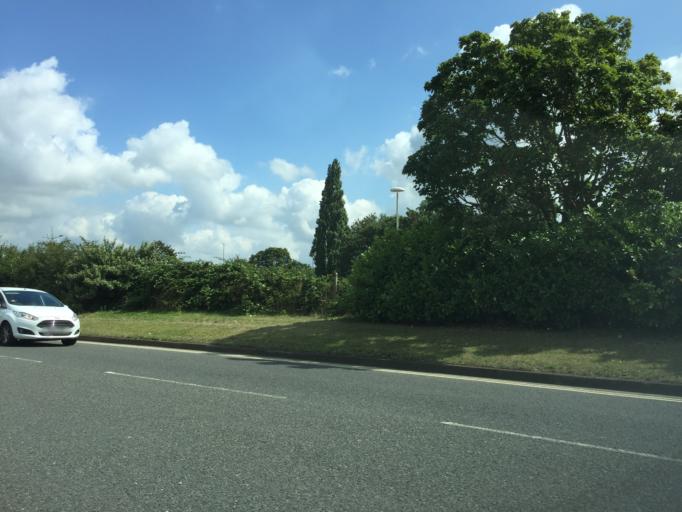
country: GB
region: England
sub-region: Gloucestershire
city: Gloucester
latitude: 51.8689
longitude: -2.2528
